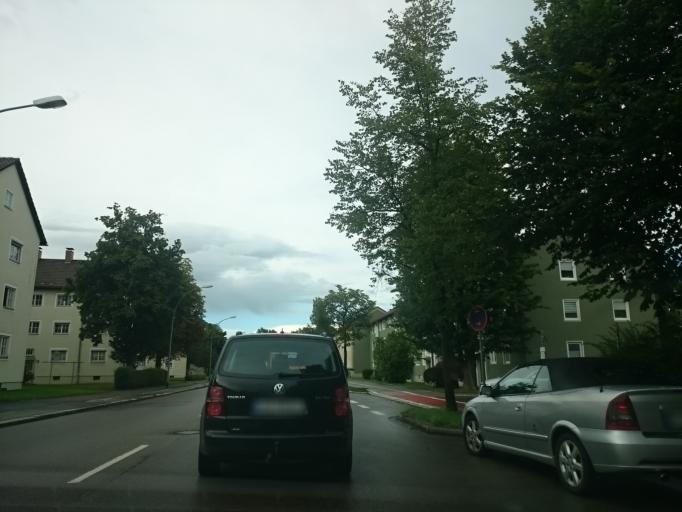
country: DE
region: Bavaria
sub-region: Swabia
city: Kempten (Allgaeu)
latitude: 47.7337
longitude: 10.3146
